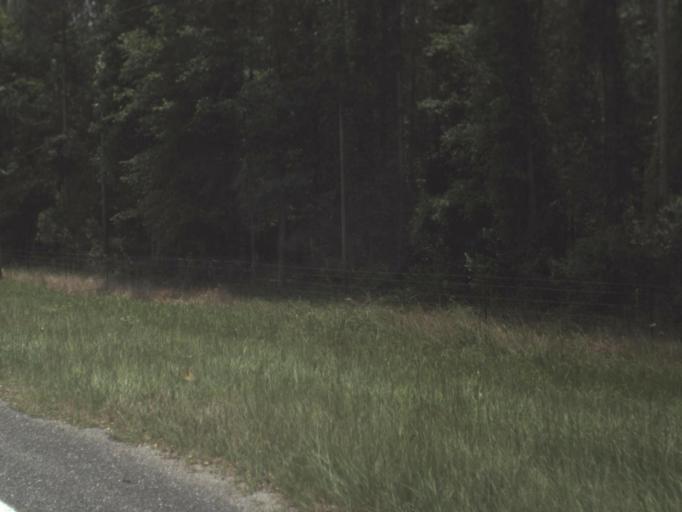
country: US
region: Florida
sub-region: Bradford County
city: Starke
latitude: 29.9636
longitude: -82.1812
